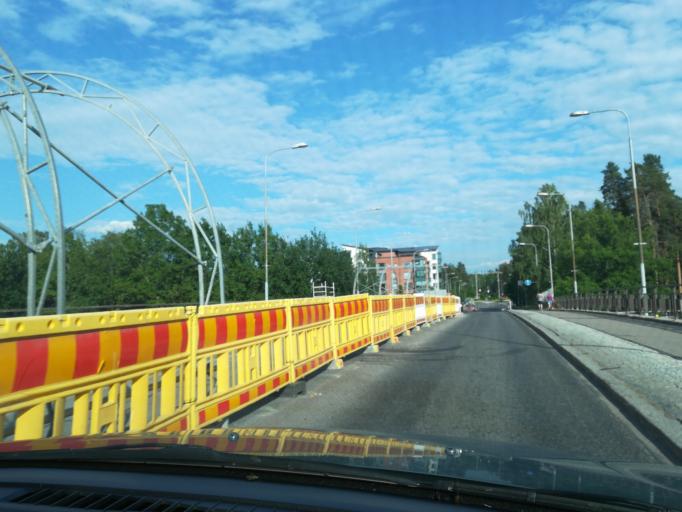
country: FI
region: South Karelia
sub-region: Imatra
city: Imatra
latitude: 61.1685
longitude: 28.7763
